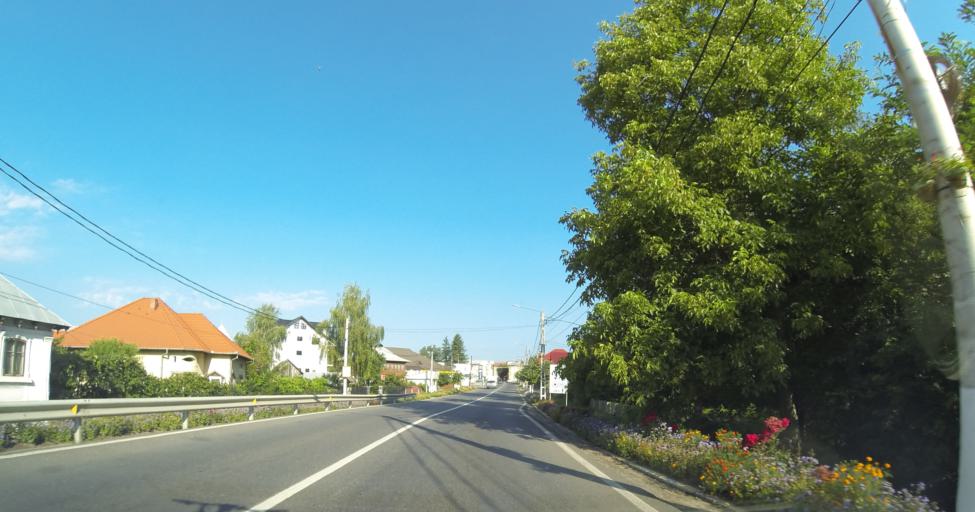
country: RO
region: Valcea
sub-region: Comuna Horezu
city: Horezu
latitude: 45.1449
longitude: 23.9954
